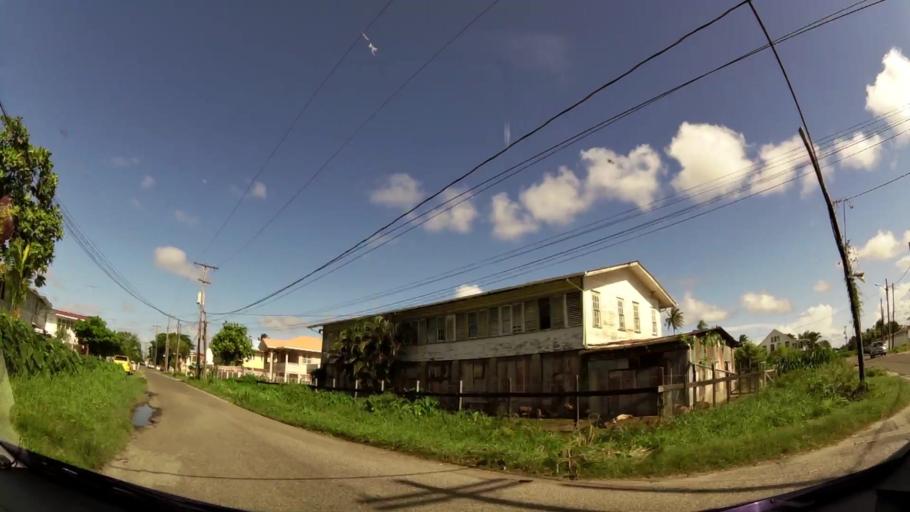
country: GY
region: Demerara-Mahaica
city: Georgetown
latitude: 6.8228
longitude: -58.1301
